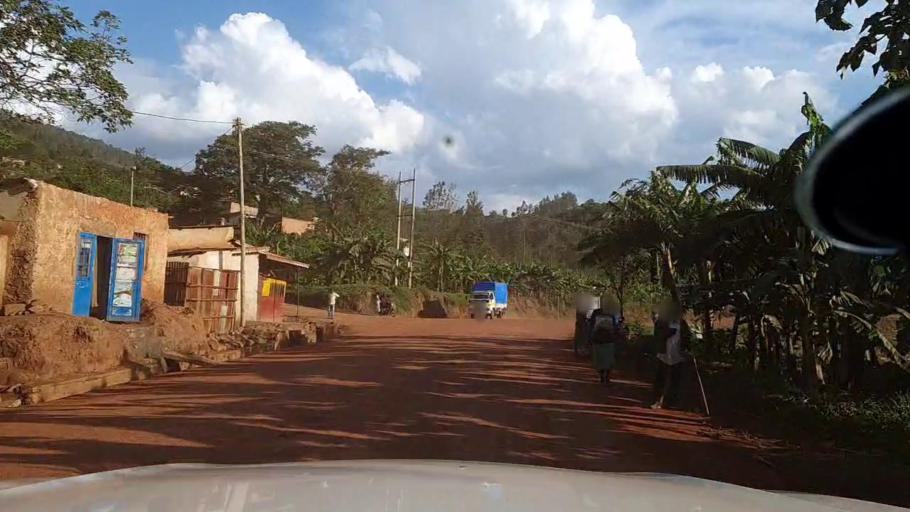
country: RW
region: Kigali
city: Kigali
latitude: -1.9177
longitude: 29.9902
